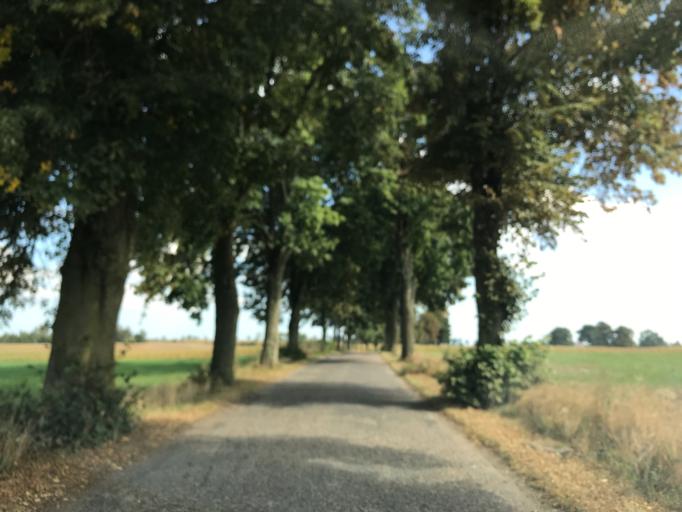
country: PL
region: Kujawsko-Pomorskie
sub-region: Powiat brodnicki
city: Brzozie
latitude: 53.3543
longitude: 19.6730
